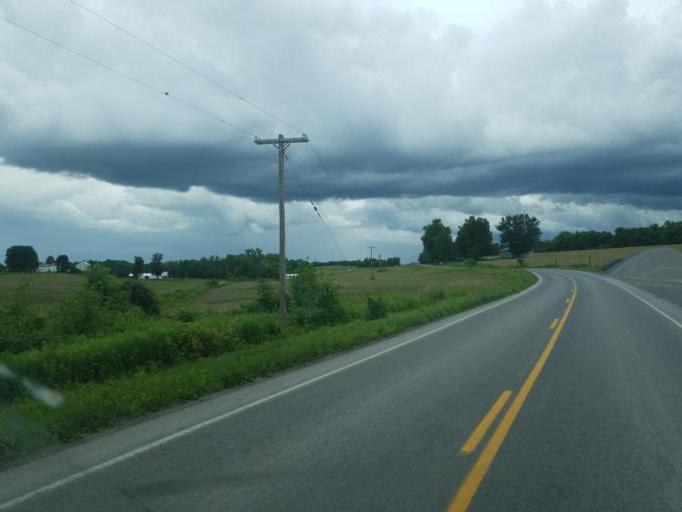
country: US
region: New York
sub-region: Wayne County
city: Clyde
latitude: 43.0360
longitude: -76.9060
